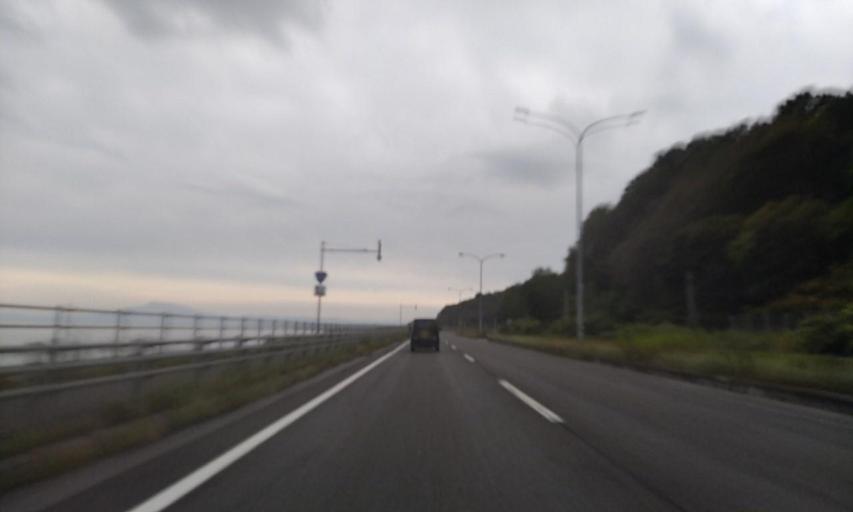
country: JP
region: Hokkaido
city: Abashiri
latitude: 44.0007
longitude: 144.2902
